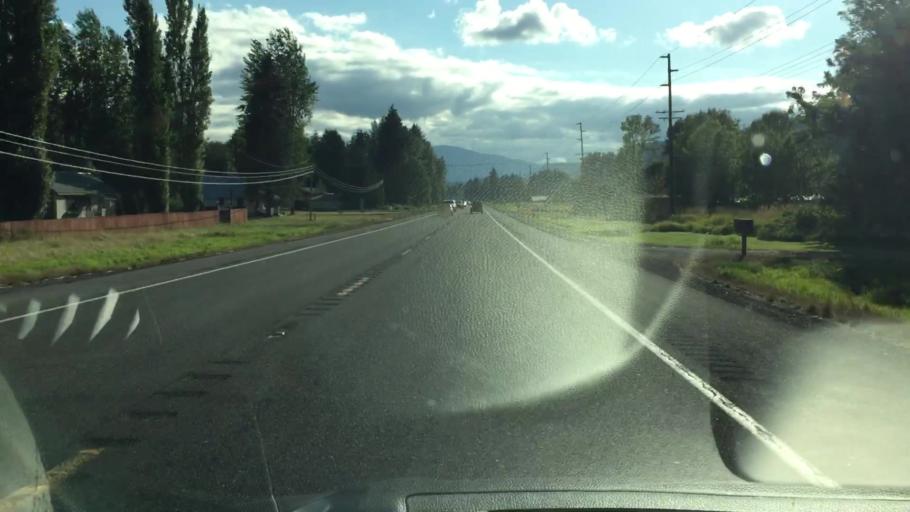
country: US
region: Washington
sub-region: Lewis County
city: Morton
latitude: 46.5290
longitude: -122.1346
